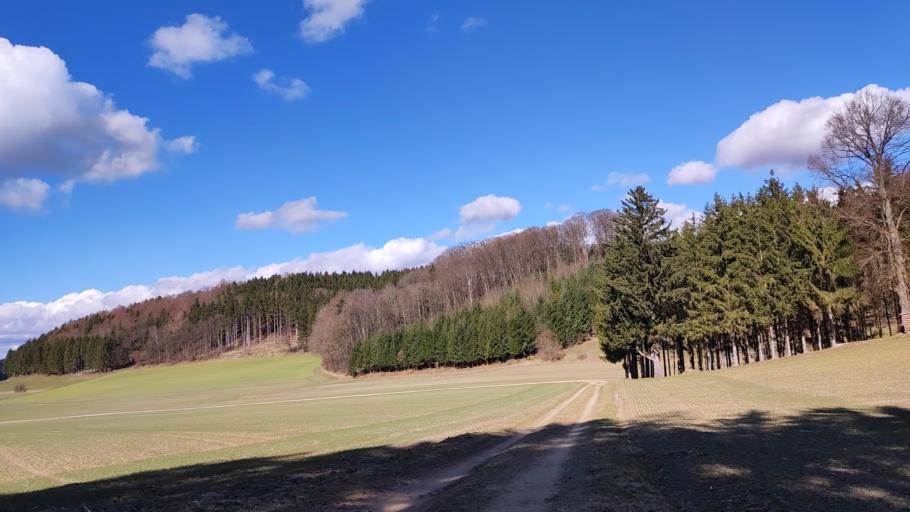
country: DE
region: Bavaria
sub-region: Swabia
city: Zusmarshausen
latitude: 48.4292
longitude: 10.6128
